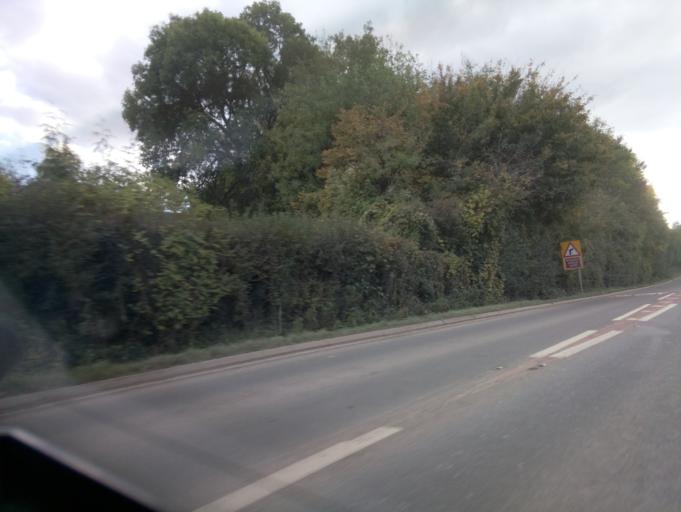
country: GB
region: England
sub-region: Herefordshire
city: Ocle Pychard
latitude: 52.0642
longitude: -2.5856
